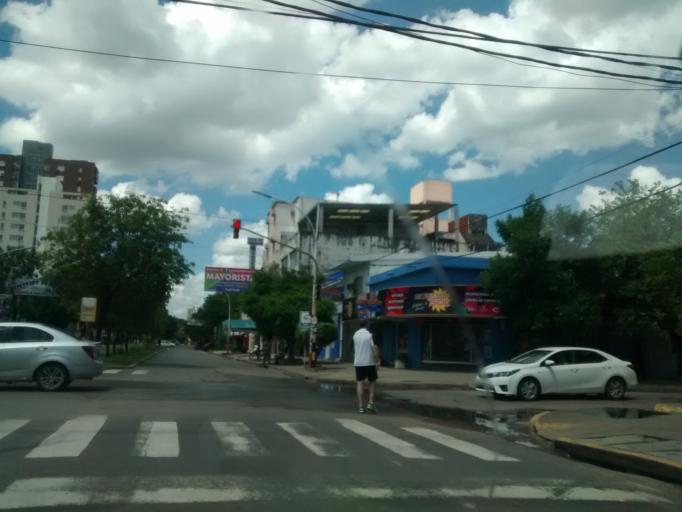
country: AR
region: Chaco
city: Resistencia
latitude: -27.4544
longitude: -58.9901
